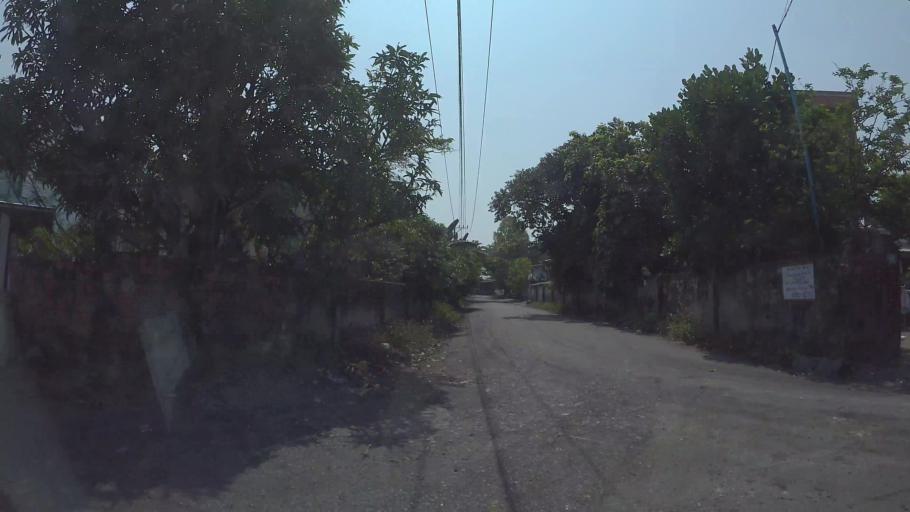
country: VN
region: Da Nang
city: Ngu Hanh Son
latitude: 15.9885
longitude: 108.2546
